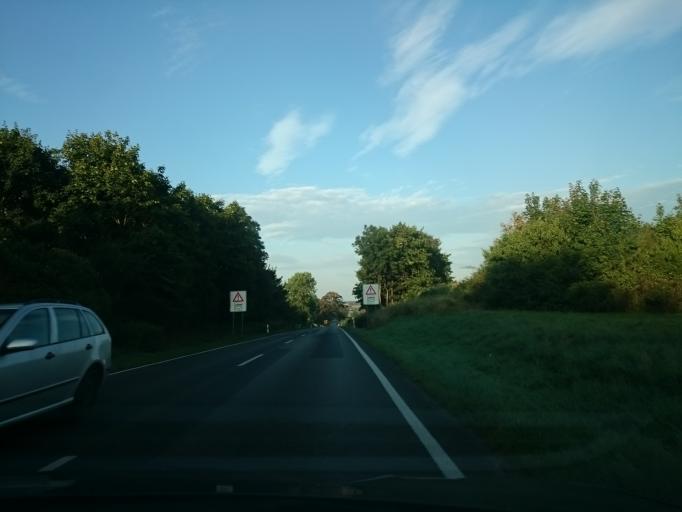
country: DE
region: Mecklenburg-Vorpommern
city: Wolgast
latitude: 54.0462
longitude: 13.7488
